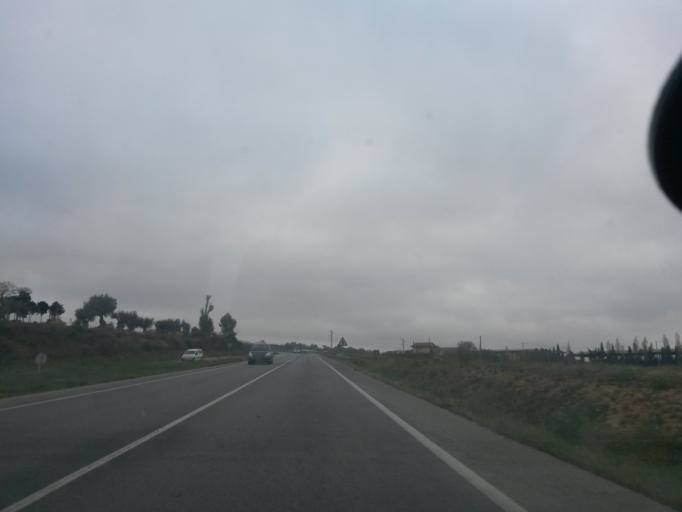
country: ES
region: Catalonia
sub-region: Provincia de Girona
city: Fontcoberta
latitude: 42.1218
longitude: 2.7851
